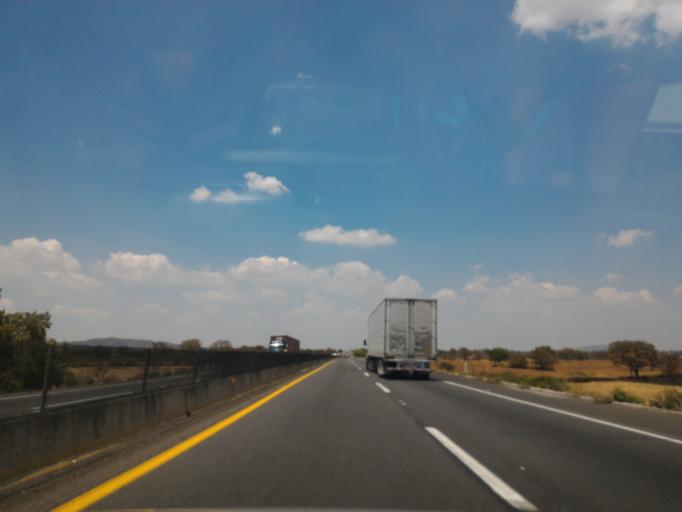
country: MX
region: Jalisco
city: Tepatitlan de Morelos
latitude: 20.8602
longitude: -102.7647
